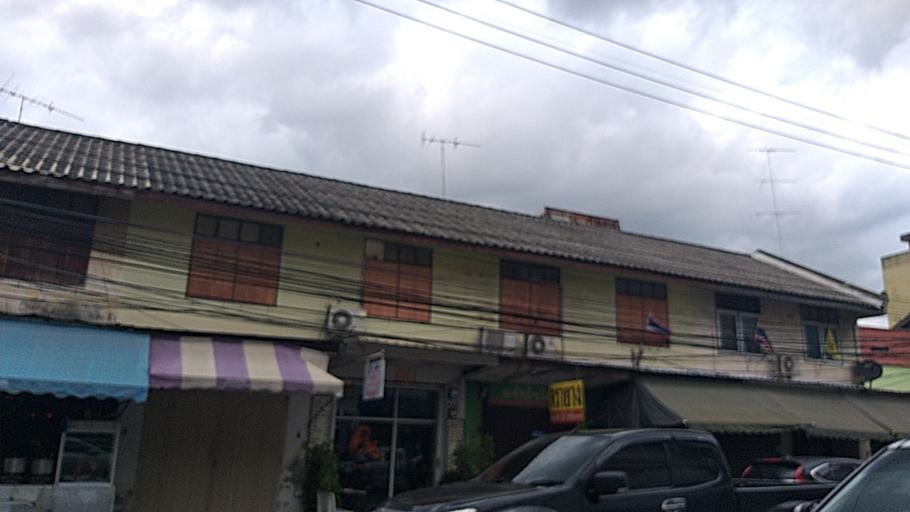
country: TH
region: Nakhon Pathom
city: Nakhon Pathom
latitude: 13.8224
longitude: 100.0516
